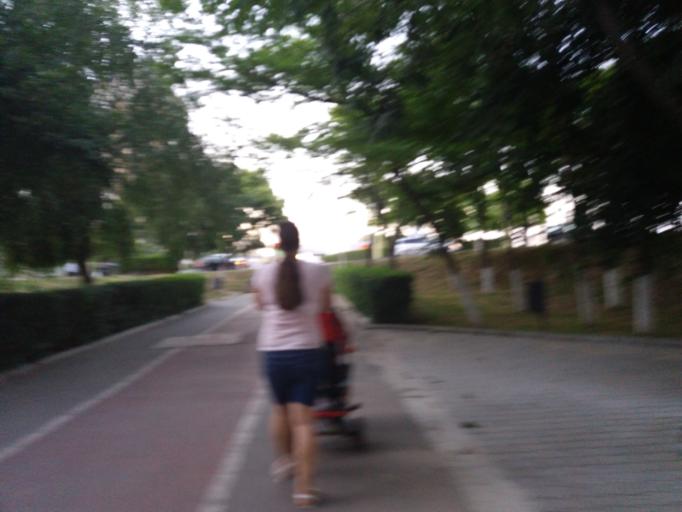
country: RO
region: Constanta
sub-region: Comuna Navodari
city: Navodari
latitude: 44.3197
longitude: 28.6171
